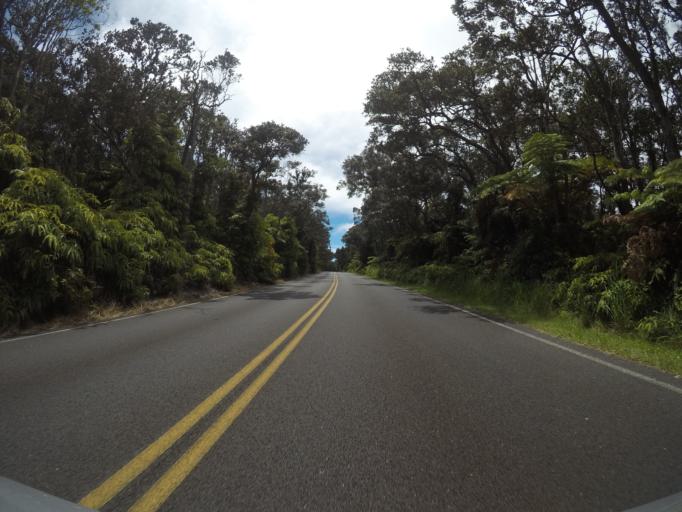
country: US
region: Hawaii
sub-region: Hawaii County
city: Volcano
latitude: 19.4255
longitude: -155.2516
